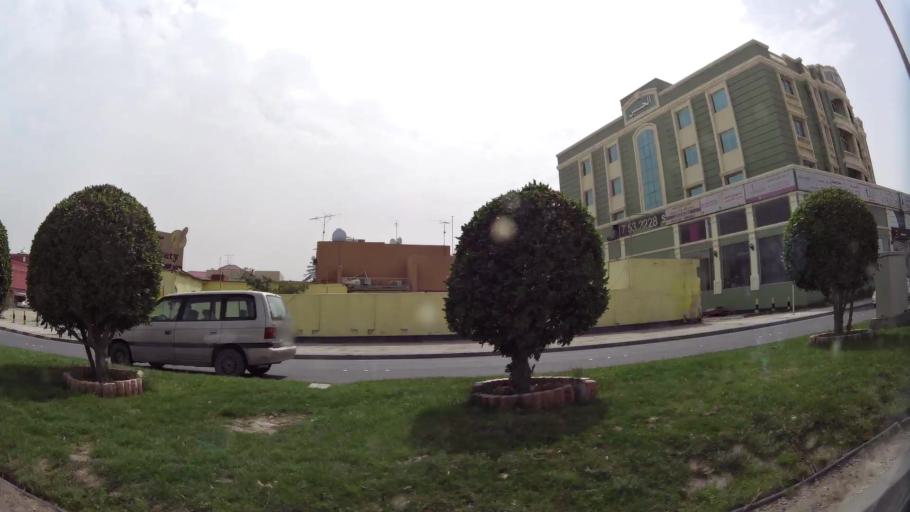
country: BH
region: Northern
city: Ar Rifa'
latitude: 26.1307
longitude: 50.5483
